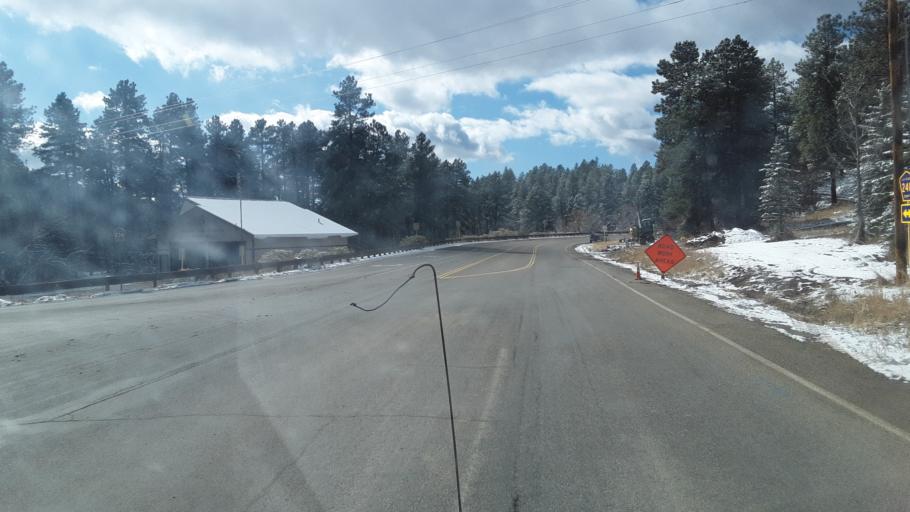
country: US
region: Colorado
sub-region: La Plata County
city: Durango
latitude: 37.3122
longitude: -107.7770
